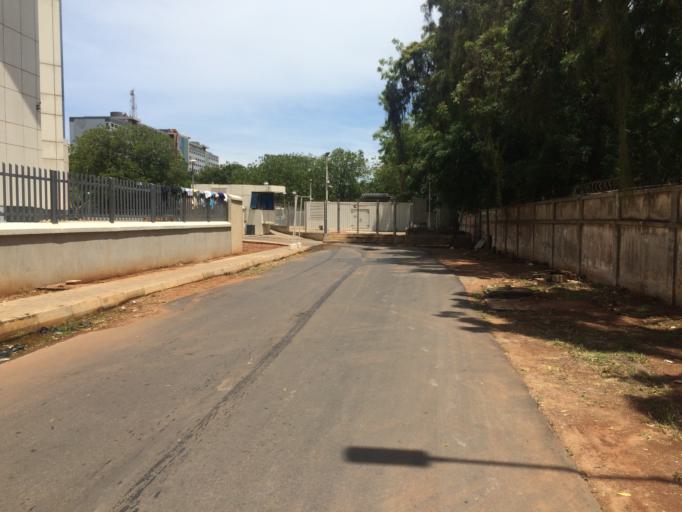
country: GH
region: Greater Accra
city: Accra
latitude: 5.5592
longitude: -0.1930
